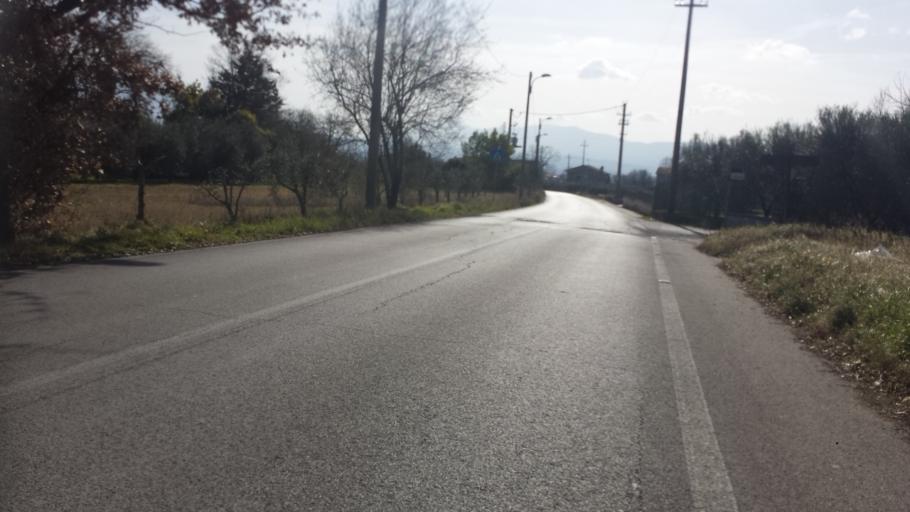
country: IT
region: Umbria
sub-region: Provincia di Terni
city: San Gemini
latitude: 42.5859
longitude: 12.5798
